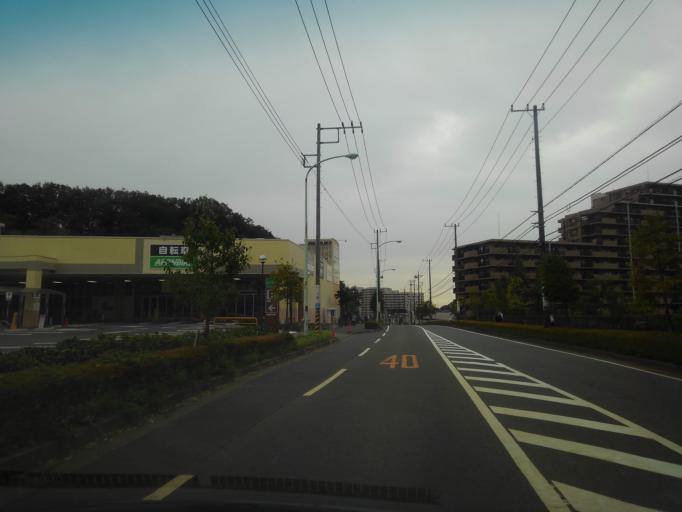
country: JP
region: Tokyo
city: Hachioji
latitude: 35.6040
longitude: 139.3603
